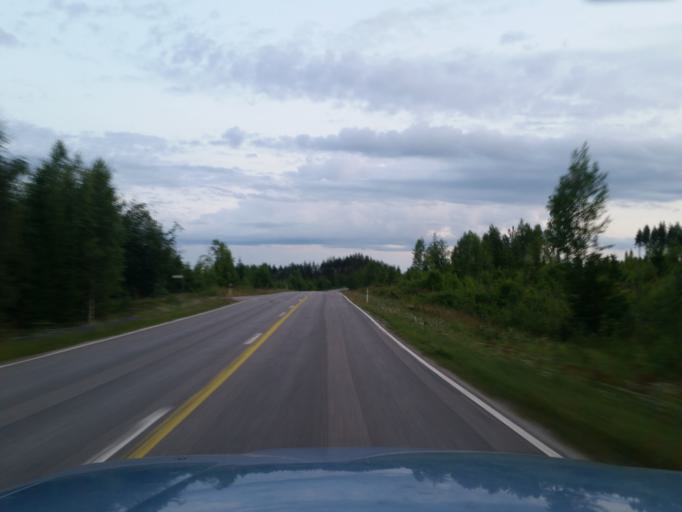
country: FI
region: Southern Savonia
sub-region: Savonlinna
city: Sulkava
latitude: 61.8136
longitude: 28.4317
